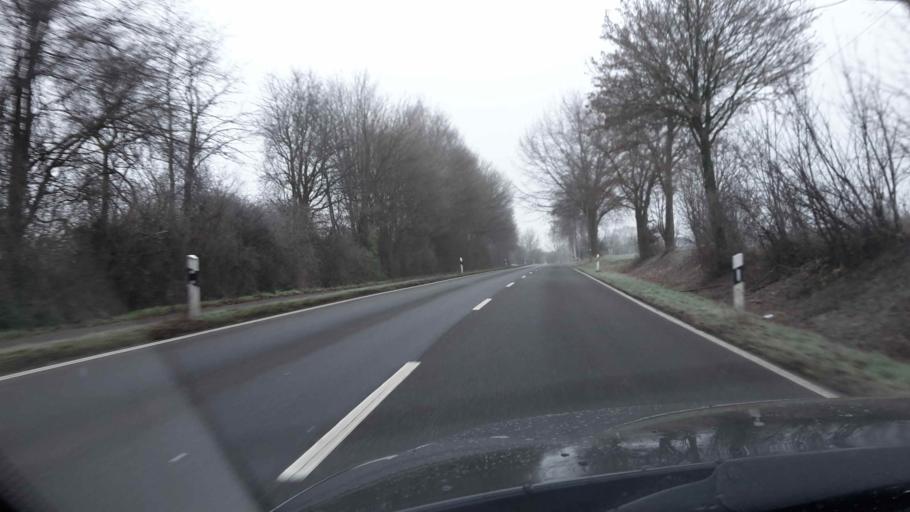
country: DE
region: North Rhine-Westphalia
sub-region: Regierungsbezirk Koln
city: Hennef
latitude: 50.7362
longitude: 7.2892
